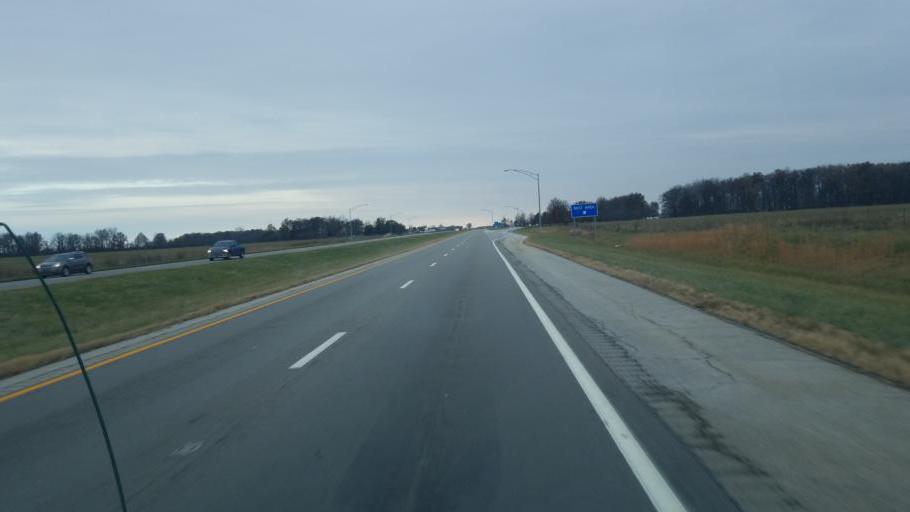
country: US
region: Ohio
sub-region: Auglaize County
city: Saint Marys
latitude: 40.5587
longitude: -84.3200
